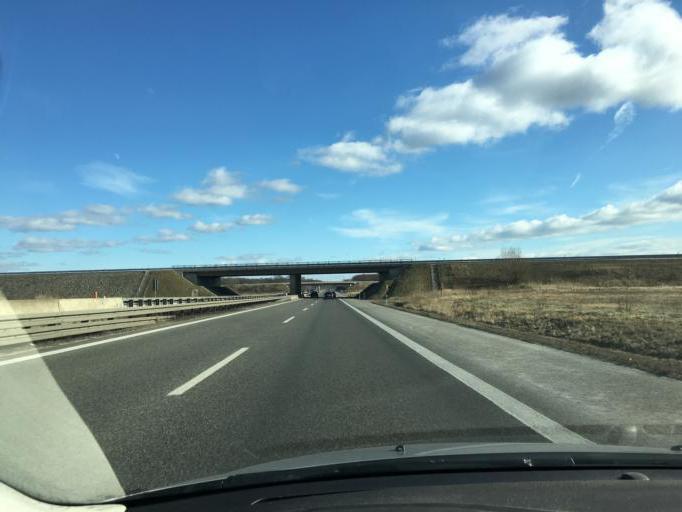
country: DE
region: Saxony
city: Borsdorf
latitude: 51.3108
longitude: 12.5514
